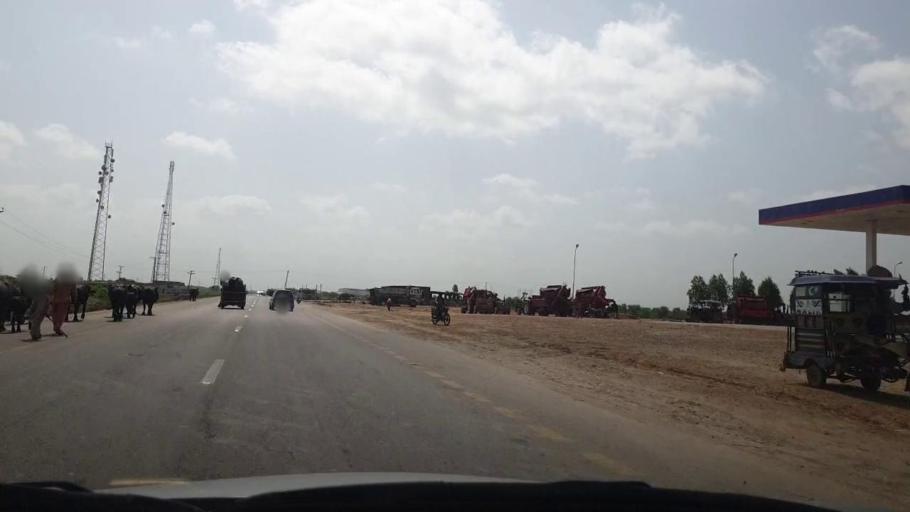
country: PK
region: Sindh
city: Matli
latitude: 24.9417
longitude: 68.7028
